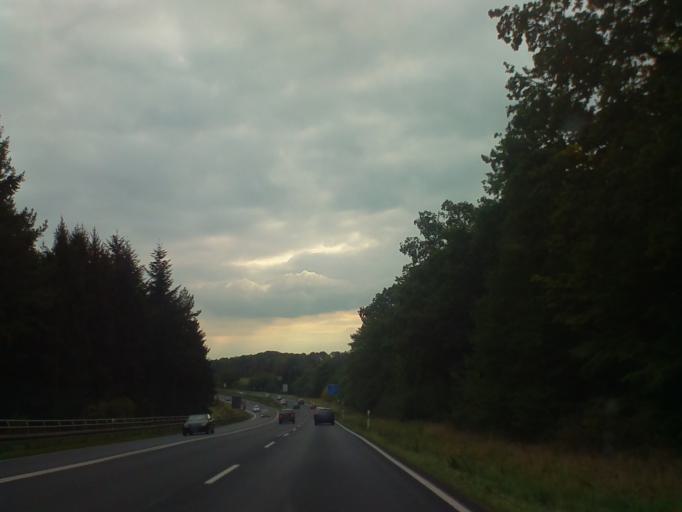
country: DE
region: Hesse
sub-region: Regierungsbezirk Kassel
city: Petersberg
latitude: 50.5889
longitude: 9.7110
